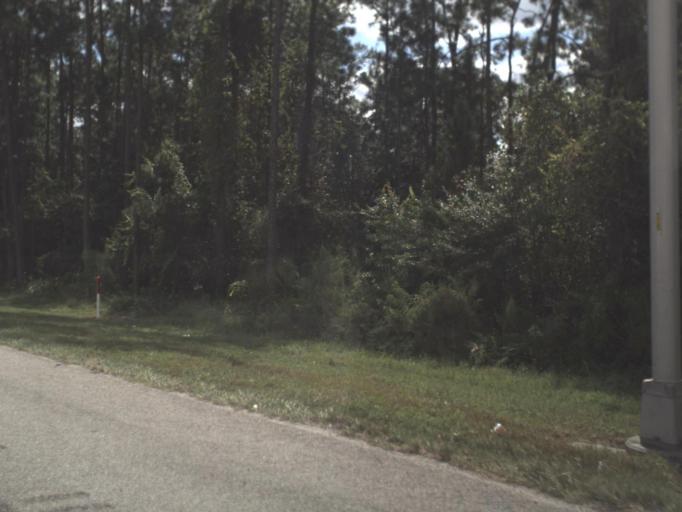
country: US
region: Florida
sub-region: Orange County
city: Tangelo Park
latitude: 28.4647
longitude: -81.4367
